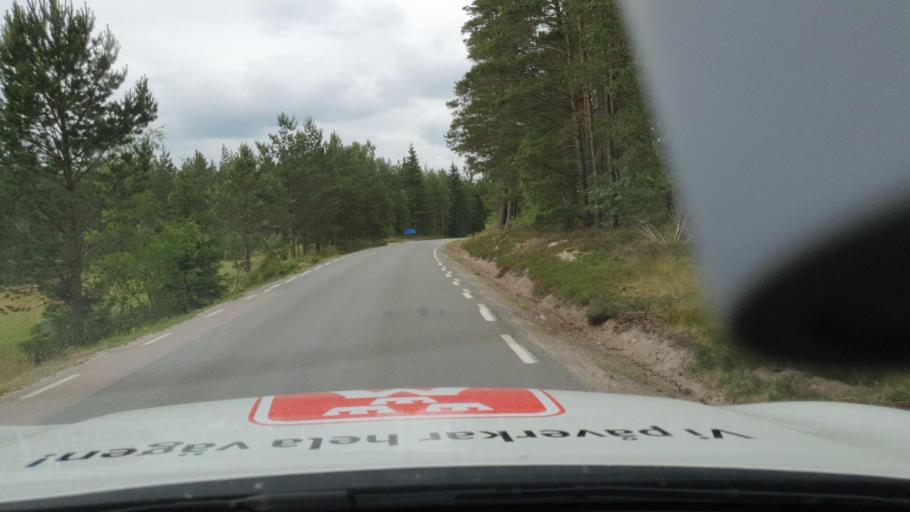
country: SE
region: Vaestra Goetaland
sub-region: Tidaholms Kommun
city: Olofstorp
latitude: 58.2617
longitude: 14.0975
